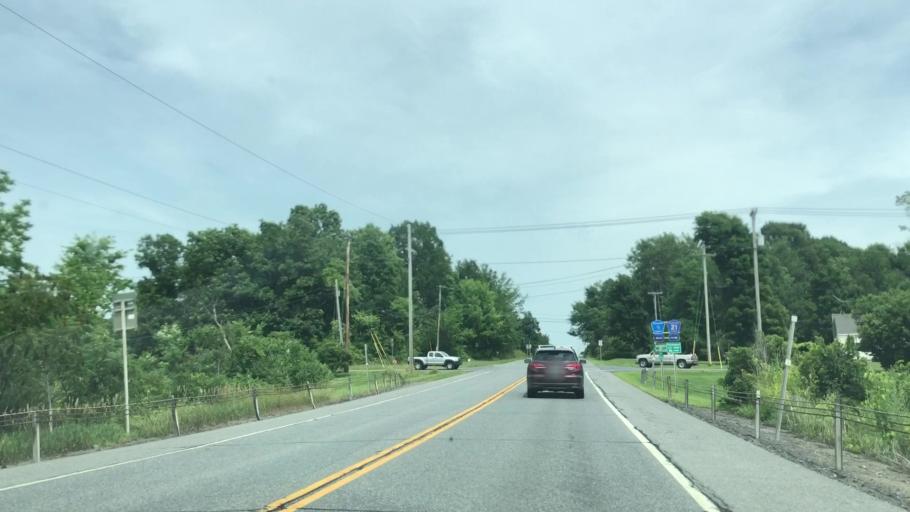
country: US
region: Vermont
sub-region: Rutland County
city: Fair Haven
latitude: 43.5672
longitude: -73.3245
